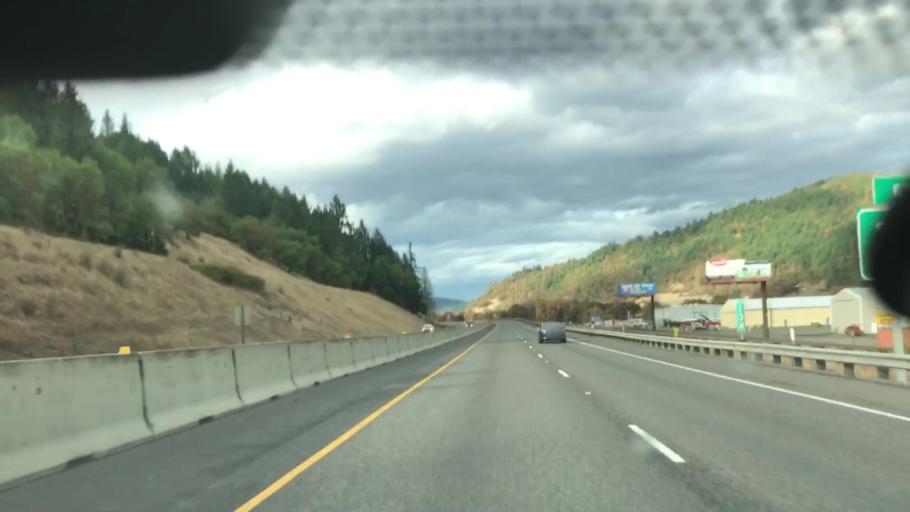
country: US
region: Oregon
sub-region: Douglas County
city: Sutherlin
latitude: 43.3514
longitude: -123.3283
